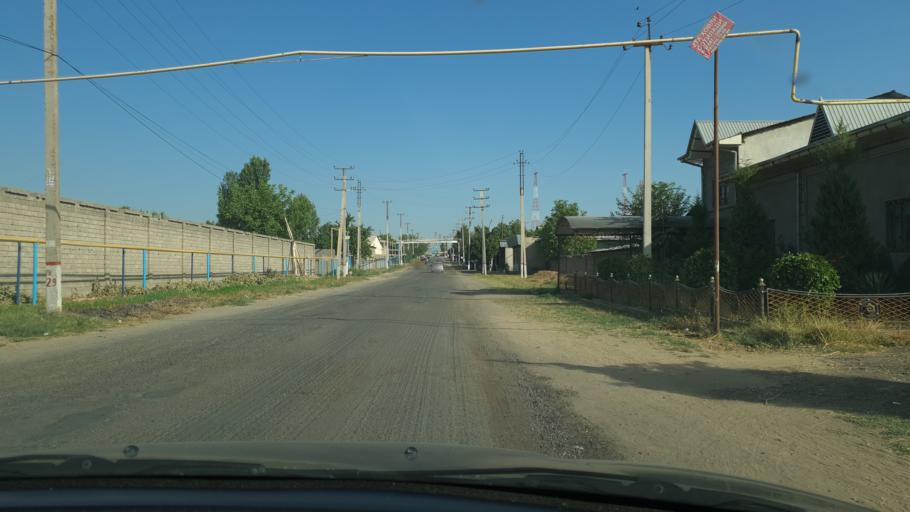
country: UZ
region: Toshkent
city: Urtaowul
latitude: 41.2049
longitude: 69.1510
